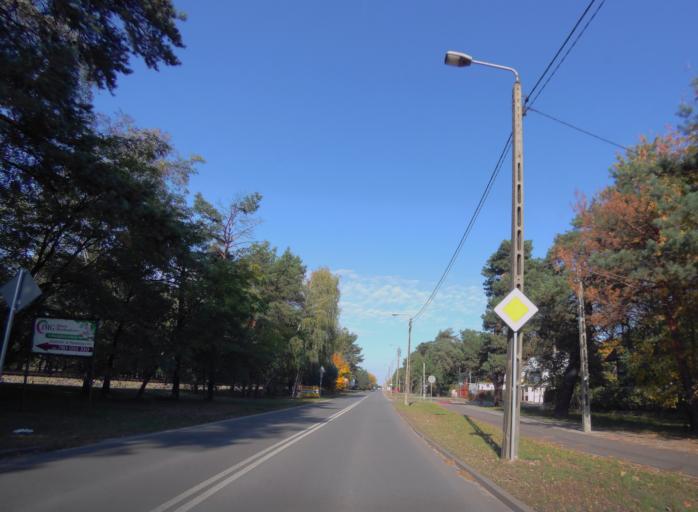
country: PL
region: Masovian Voivodeship
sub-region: Powiat otwocki
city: Jozefow
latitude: 52.1500
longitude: 21.2233
